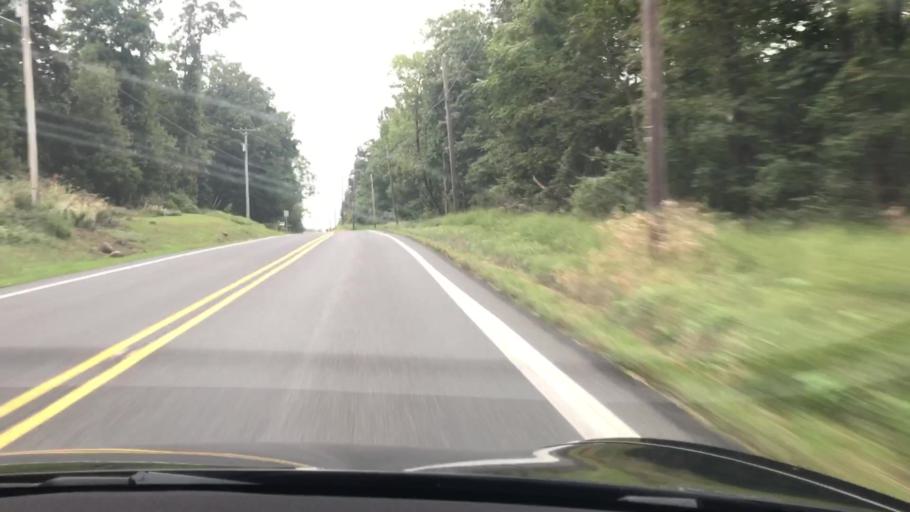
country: US
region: Pennsylvania
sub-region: Adams County
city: Lake Meade
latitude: 39.9495
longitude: -77.1297
